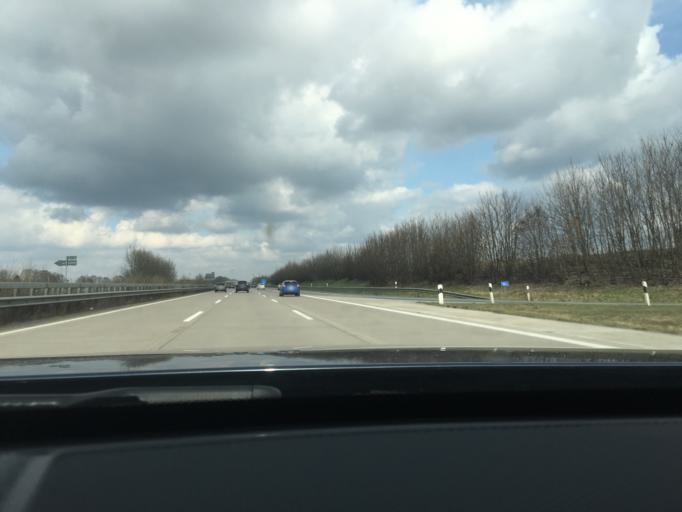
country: DE
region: Lower Saxony
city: Buehren
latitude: 52.8140
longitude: 8.2111
